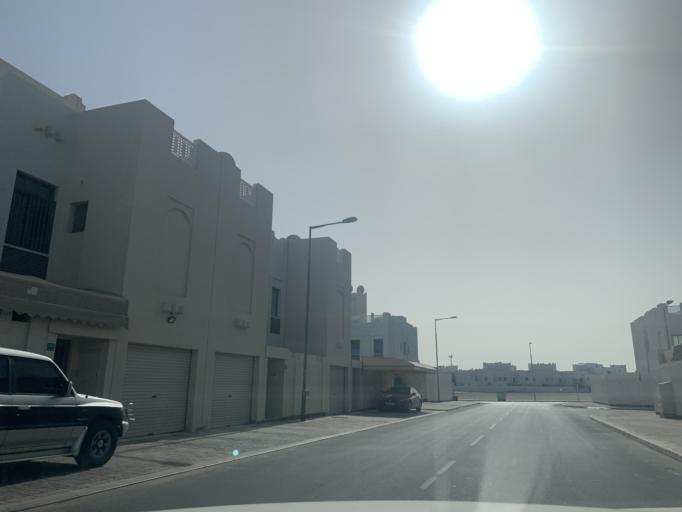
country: BH
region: Northern
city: Sitrah
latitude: 26.1604
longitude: 50.6268
